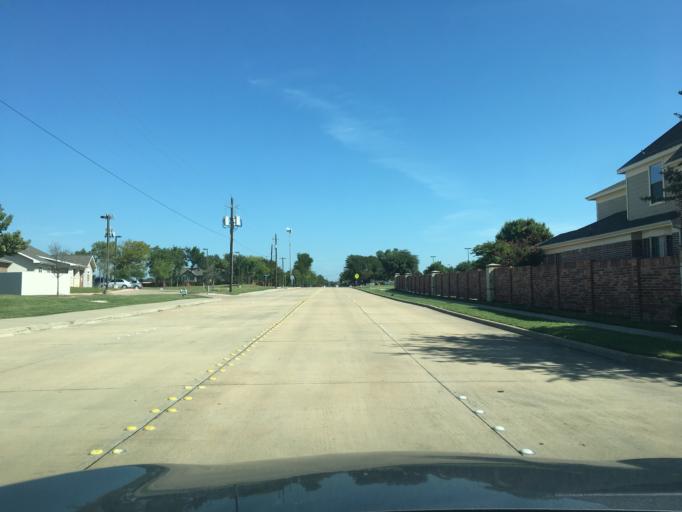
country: US
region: Texas
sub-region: Dallas County
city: Sachse
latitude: 32.9652
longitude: -96.6011
